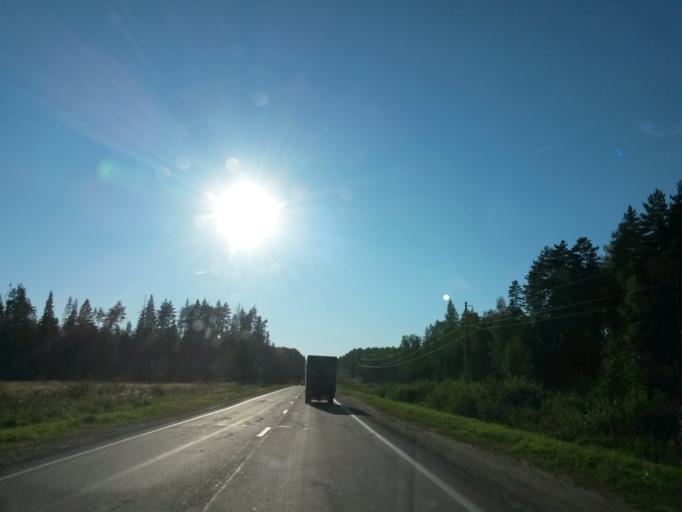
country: RU
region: Jaroslavl
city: Gavrilov-Yam
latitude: 57.2664
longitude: 39.9967
